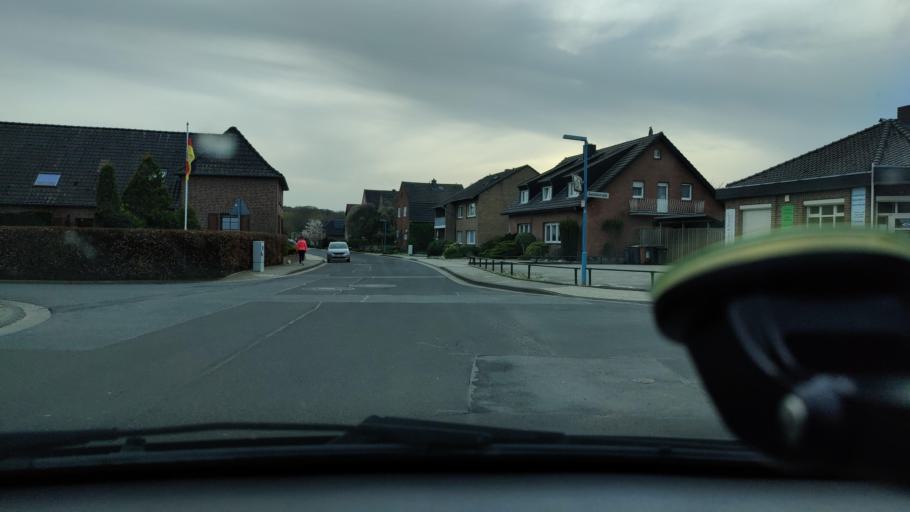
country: DE
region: North Rhine-Westphalia
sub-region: Regierungsbezirk Dusseldorf
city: Kleve
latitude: 51.7766
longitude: 6.1786
